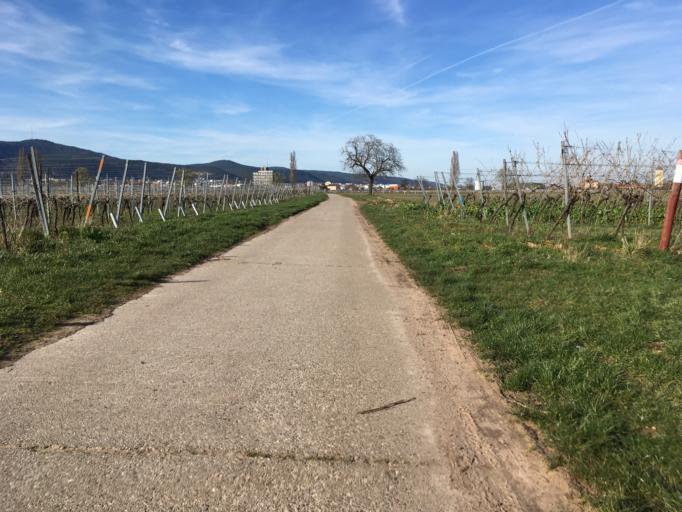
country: DE
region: Rheinland-Pfalz
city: Neustadt
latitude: 49.3322
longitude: 8.1620
